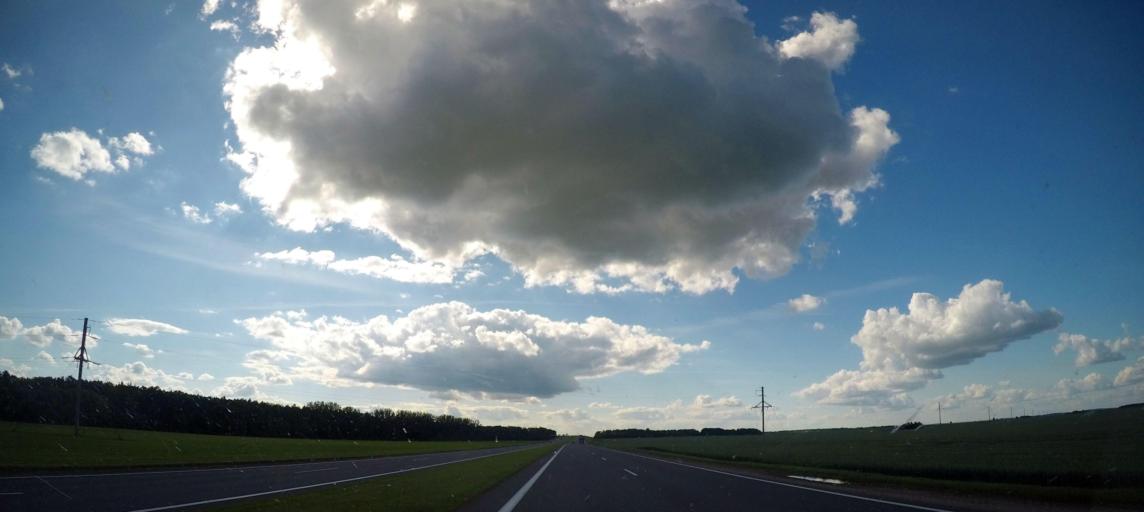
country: BY
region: Grodnenskaya
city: Skidal'
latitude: 53.5905
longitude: 24.1635
